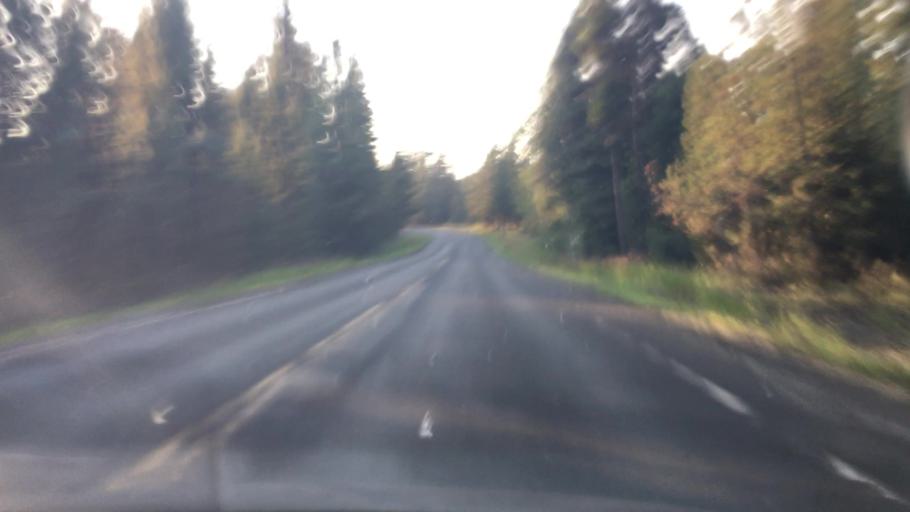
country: US
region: Idaho
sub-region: Valley County
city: McCall
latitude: 44.9233
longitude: -116.1405
